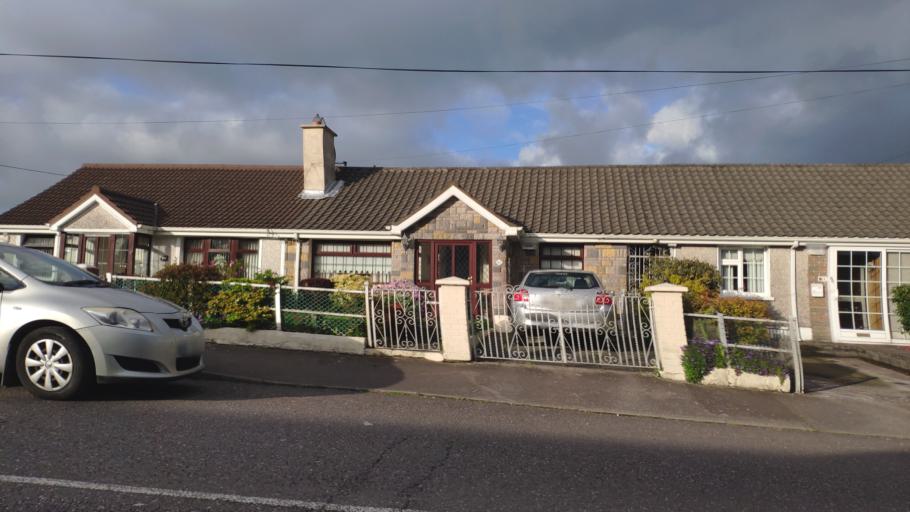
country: IE
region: Munster
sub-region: County Cork
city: Cork
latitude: 51.9120
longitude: -8.4881
